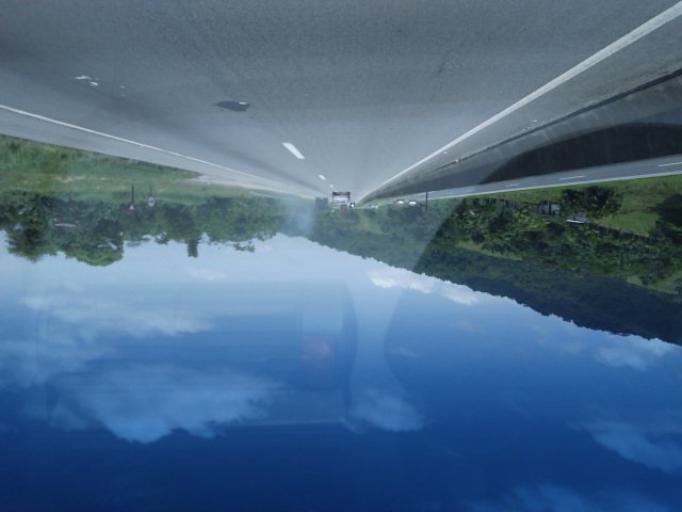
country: BR
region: Sao Paulo
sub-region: Miracatu
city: Miracatu
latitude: -24.3035
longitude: -47.4882
